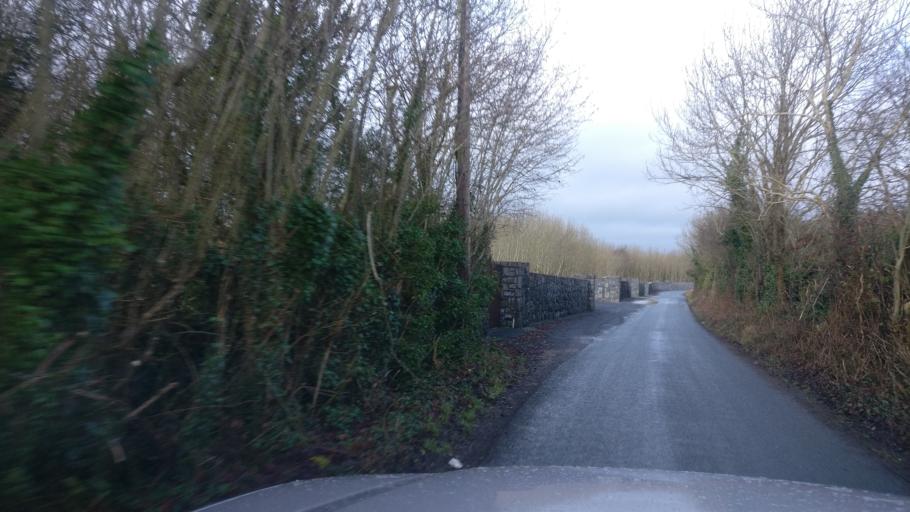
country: IE
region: Connaught
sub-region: County Galway
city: Athenry
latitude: 53.2529
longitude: -8.7224
